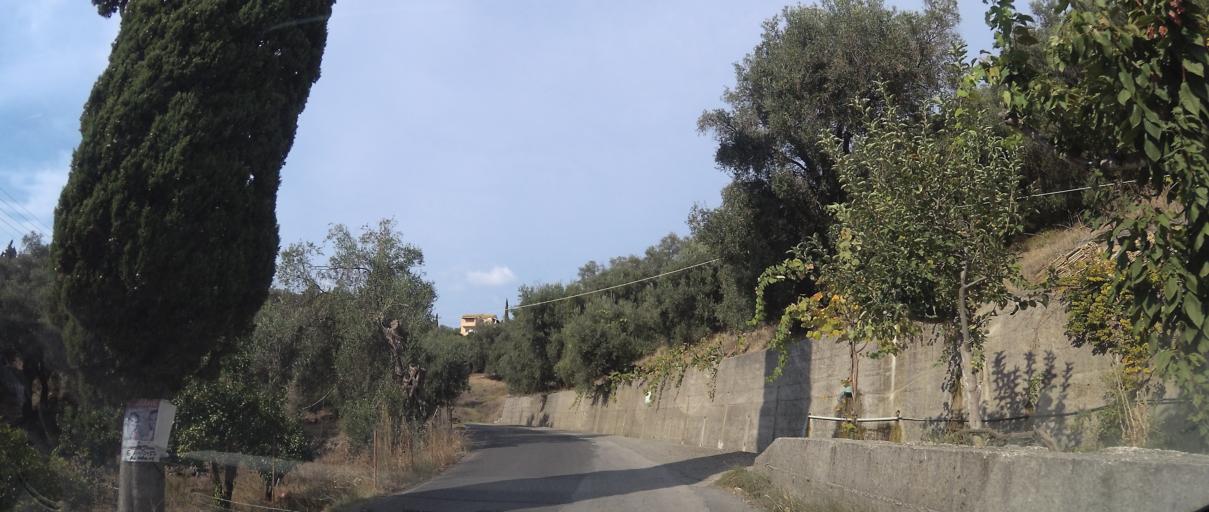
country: GR
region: Ionian Islands
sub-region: Nomos Kerkyras
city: Kynopiastes
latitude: 39.5410
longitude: 19.8712
